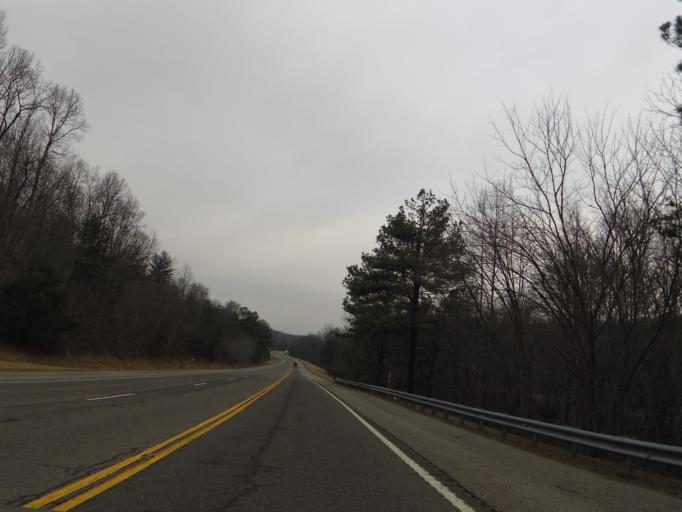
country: US
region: Tennessee
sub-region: Morgan County
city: Wartburg
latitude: 36.2274
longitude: -84.6666
